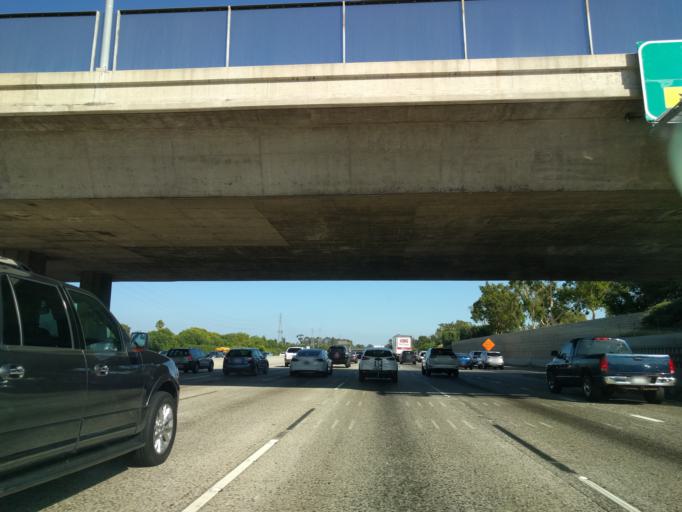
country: US
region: California
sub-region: Orange County
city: Irvine
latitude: 33.6725
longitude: -117.8322
